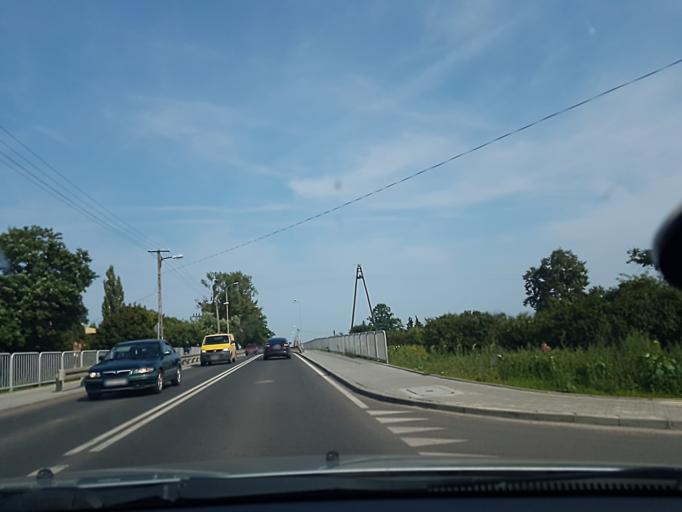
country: PL
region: Lodz Voivodeship
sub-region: Powiat zgierski
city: Zgierz
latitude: 51.8673
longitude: 19.4074
